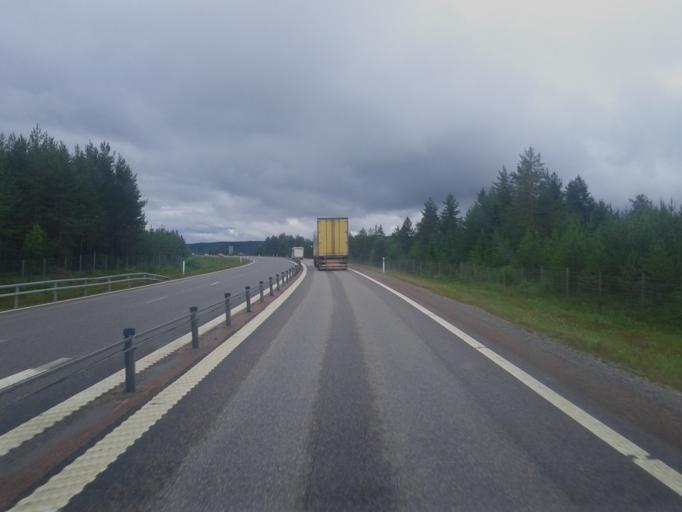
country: SE
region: Vaesternorrland
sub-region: Haernoesands Kommun
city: Haernoesand
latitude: 62.7250
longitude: 17.9226
